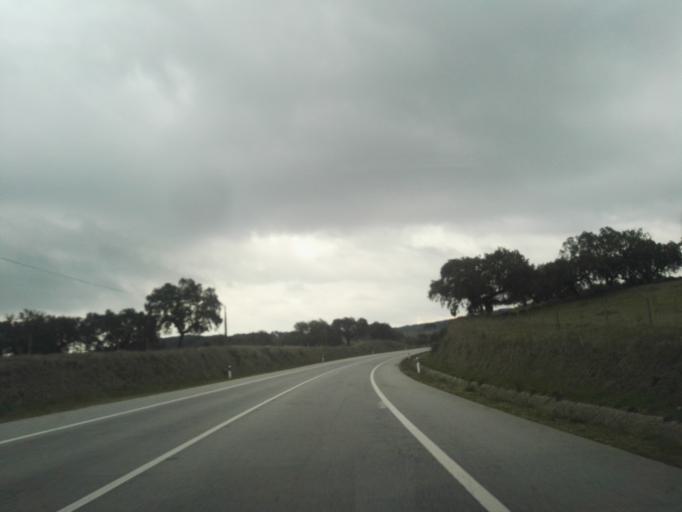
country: PT
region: Portalegre
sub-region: Portalegre
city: Alegrete
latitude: 39.1857
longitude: -7.3469
